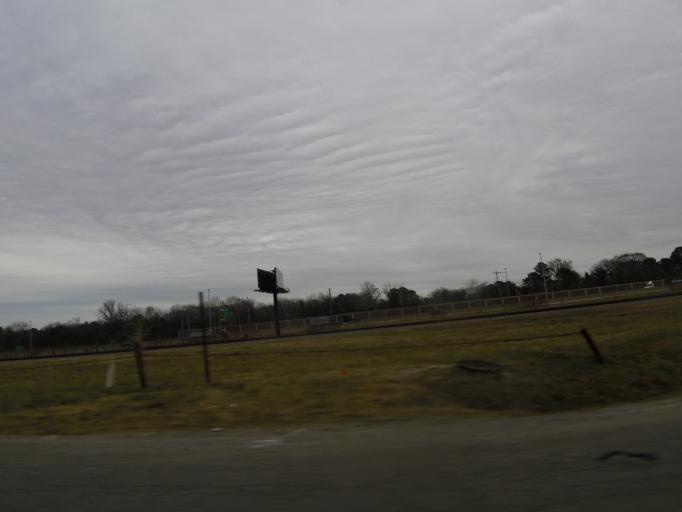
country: US
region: Virginia
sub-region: City of Portsmouth
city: Portsmouth
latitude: 36.8407
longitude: -76.3310
